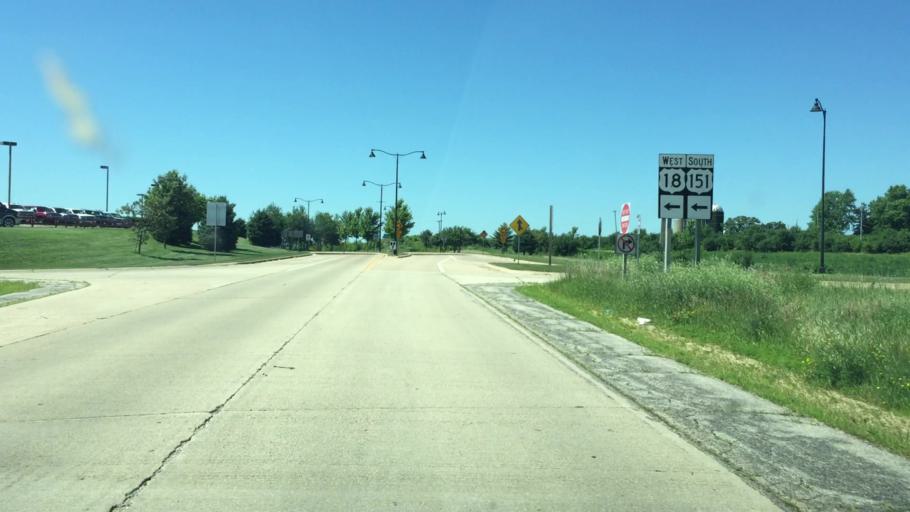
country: US
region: Wisconsin
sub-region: Dane County
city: Mount Horeb
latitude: 43.0049
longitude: -89.7028
